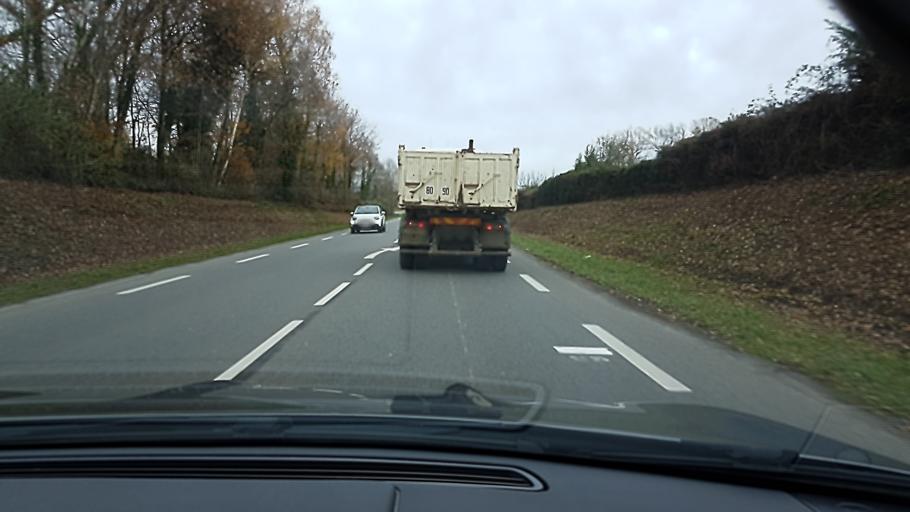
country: FR
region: Aquitaine
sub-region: Departement des Pyrenees-Atlantiques
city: Idron
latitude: 43.3124
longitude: -0.3042
